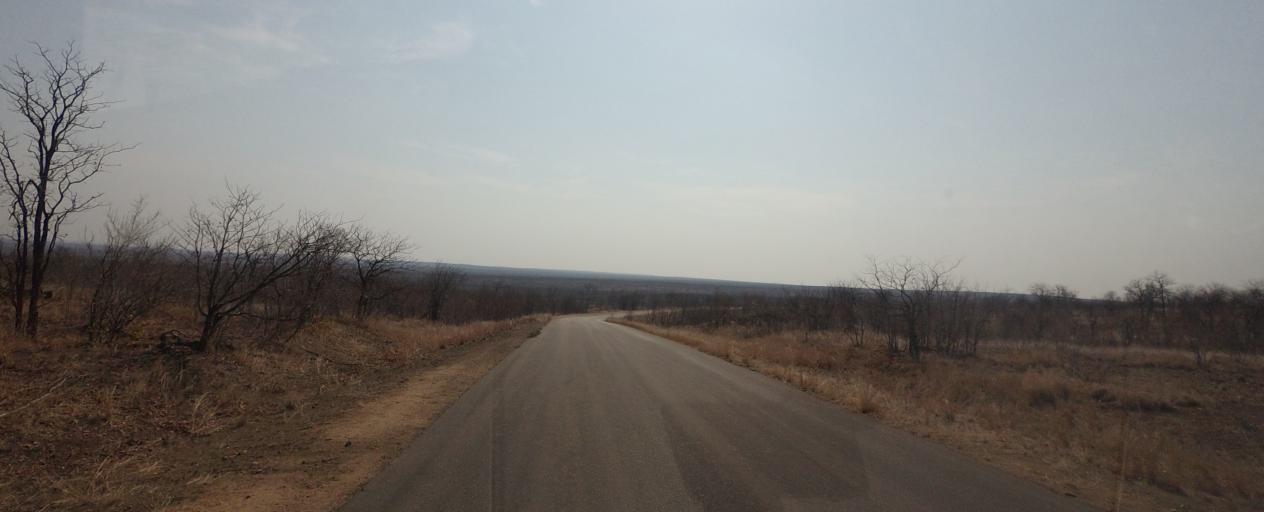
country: ZA
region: Limpopo
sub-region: Mopani District Municipality
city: Phalaborwa
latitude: -23.9711
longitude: 31.6313
